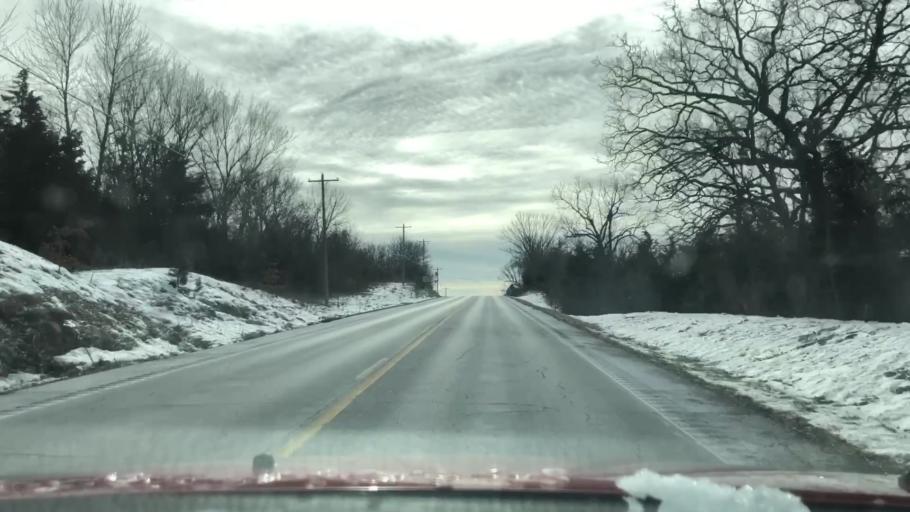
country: US
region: Missouri
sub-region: Jackson County
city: Oak Grove
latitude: 38.9702
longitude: -94.1308
